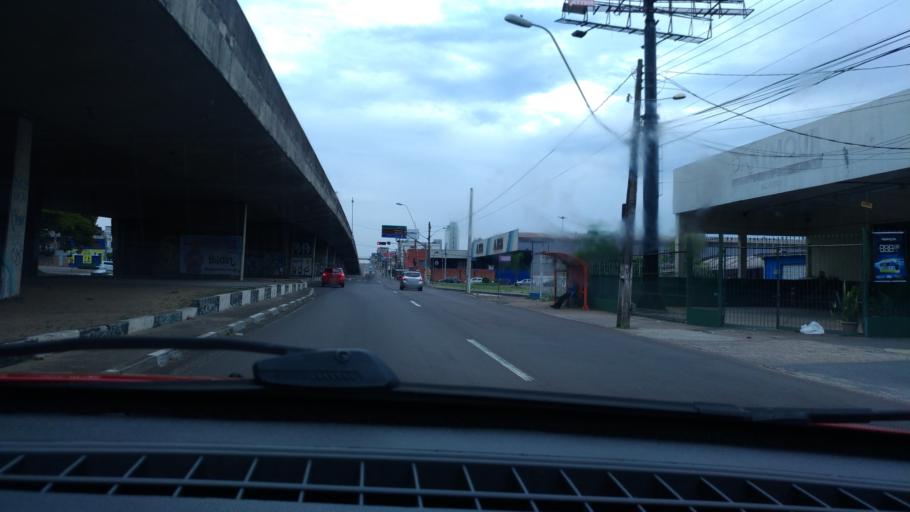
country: BR
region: Rio Grande do Sul
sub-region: Canoas
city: Canoas
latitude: -29.9024
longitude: -51.1768
